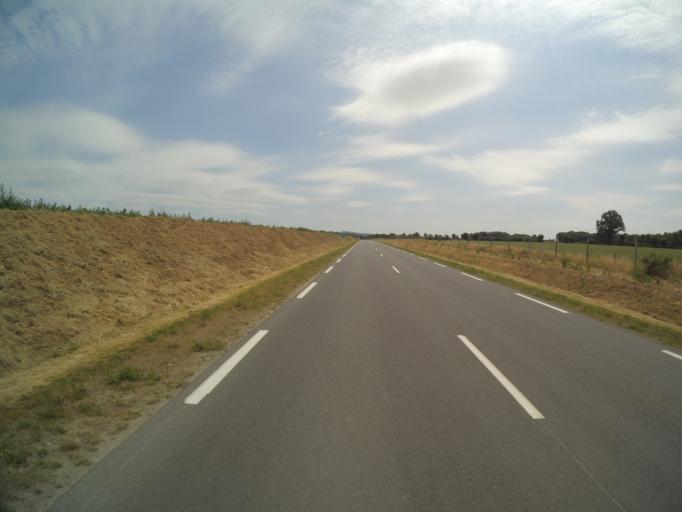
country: FR
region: Pays de la Loire
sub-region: Departement de la Vendee
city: Saint-Paul-en-Pareds
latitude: 46.8447
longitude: -1.0014
